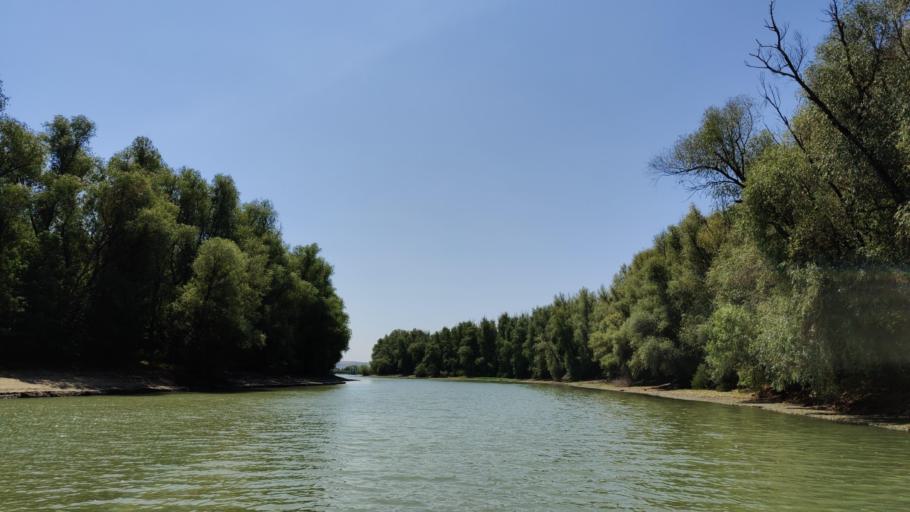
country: RO
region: Tulcea
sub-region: Municipiul Tulcea
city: Tulcea
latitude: 45.2076
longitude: 28.8548
